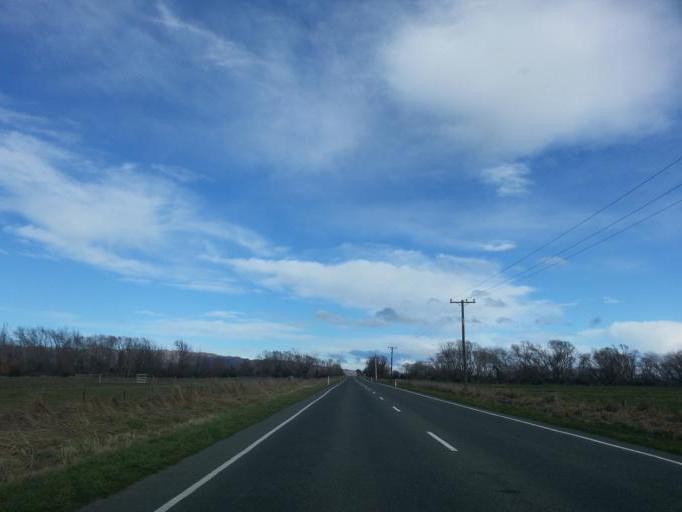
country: NZ
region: Canterbury
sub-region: Hurunui District
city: Amberley
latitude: -42.7944
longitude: 172.8317
